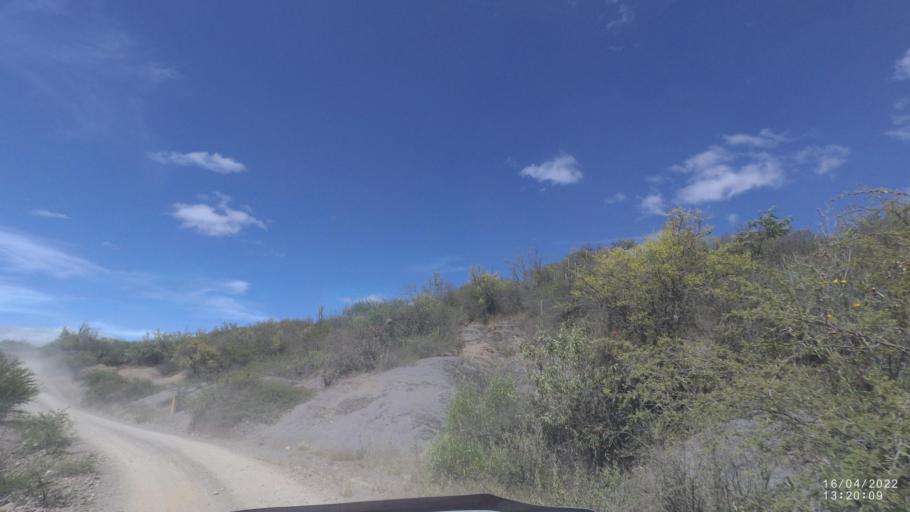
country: BO
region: Cochabamba
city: Mizque
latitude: -17.9897
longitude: -65.6143
